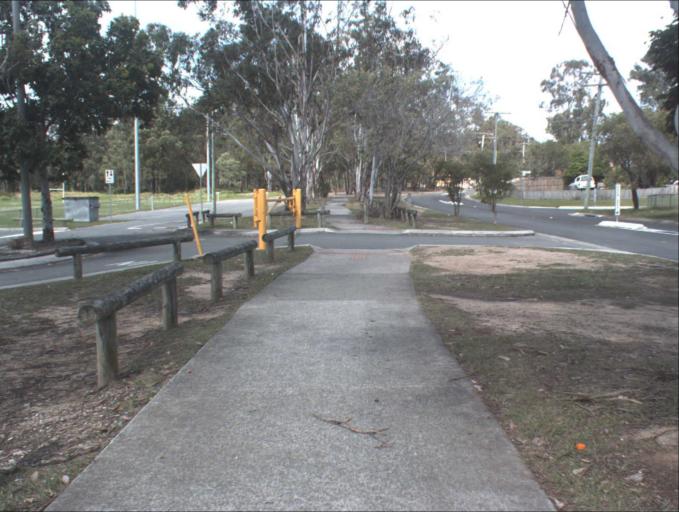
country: AU
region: Queensland
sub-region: Logan
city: Woodridge
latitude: -27.6705
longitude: 153.0586
